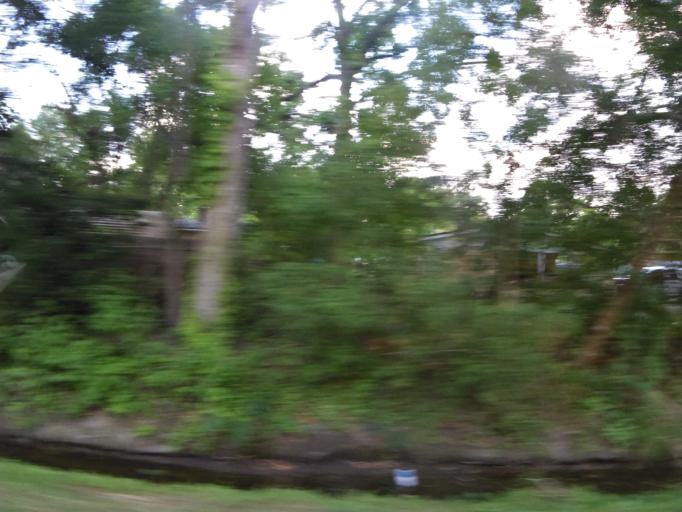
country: US
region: Florida
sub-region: Duval County
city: Jacksonville
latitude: 30.2991
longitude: -81.7391
